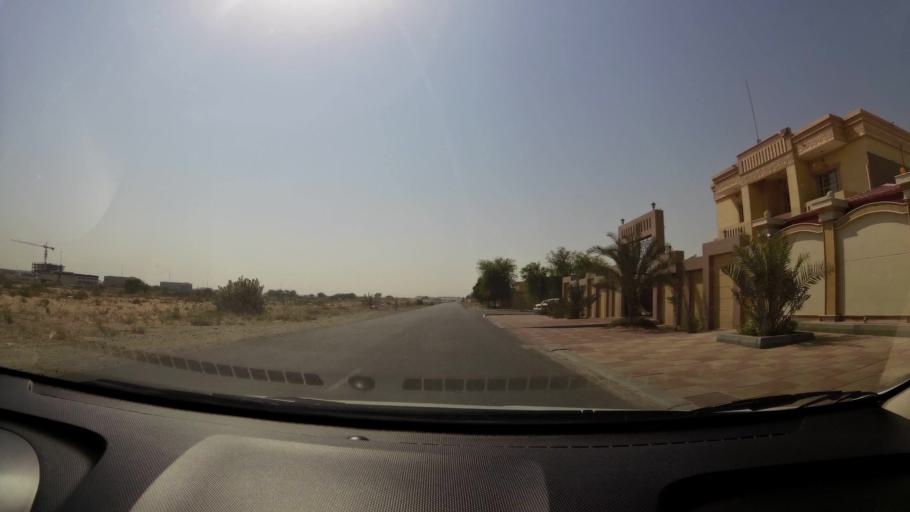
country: AE
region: Ajman
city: Ajman
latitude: 25.4174
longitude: 55.5403
